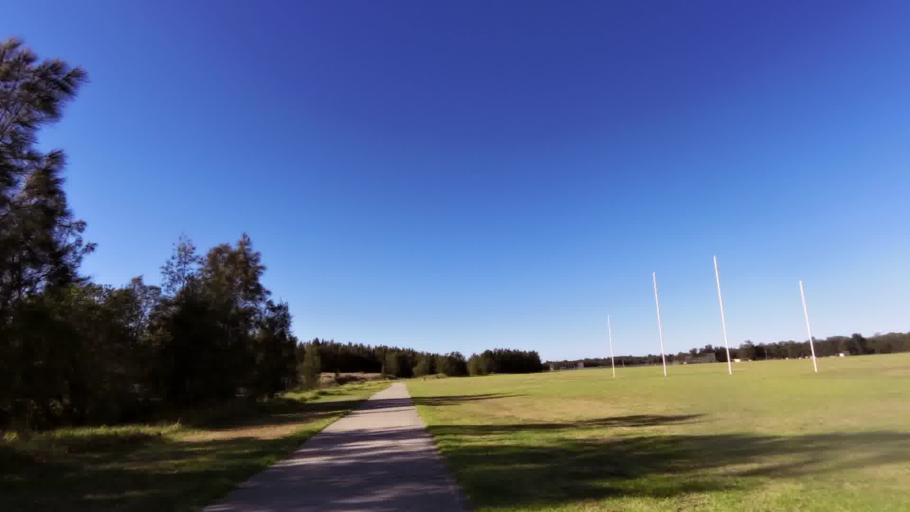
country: AU
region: New South Wales
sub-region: Wollongong
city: Berkeley
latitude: -34.4800
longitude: 150.8341
